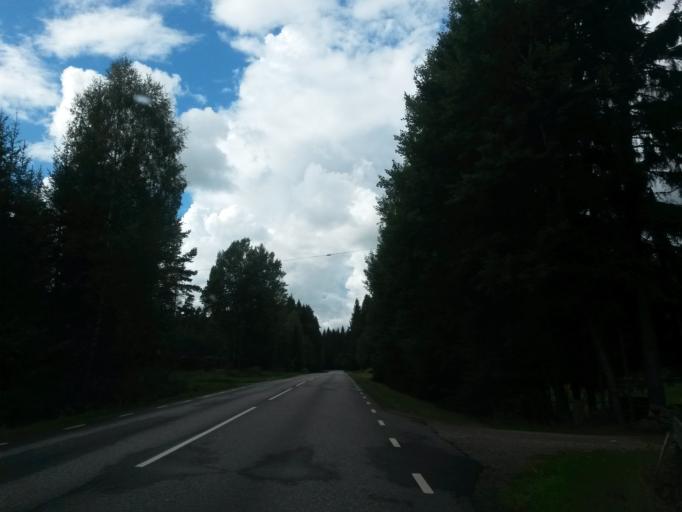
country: SE
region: Vaestra Goetaland
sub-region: Herrljunga Kommun
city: Herrljunga
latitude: 57.9919
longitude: 12.9632
